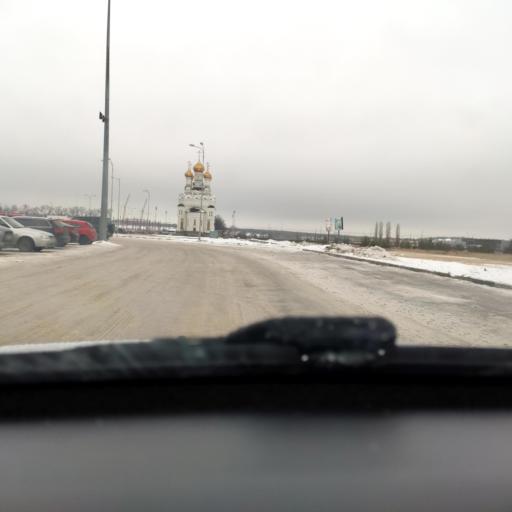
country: RU
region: Voronezj
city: Podgornoye
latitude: 51.7917
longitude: 39.2051
